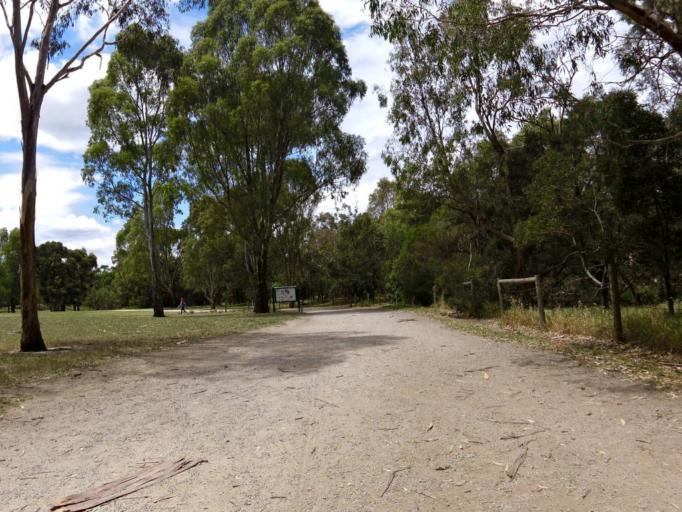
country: AU
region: Victoria
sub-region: Whitehorse
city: Burwood
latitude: -37.8445
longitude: 145.1152
